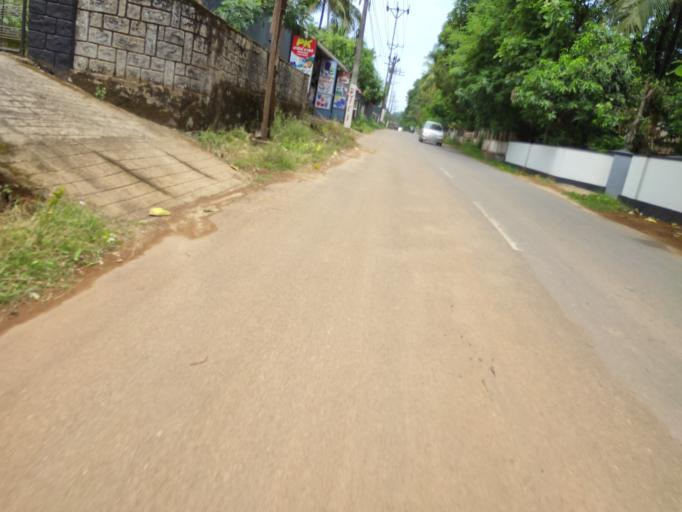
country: IN
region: Kerala
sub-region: Malappuram
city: Manjeri
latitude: 11.2139
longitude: 76.2608
